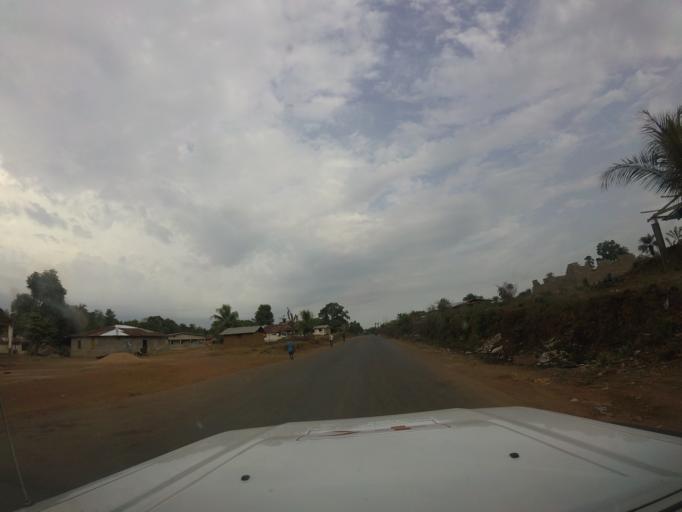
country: LR
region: Bomi
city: Tubmanburg
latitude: 6.7235
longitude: -10.9828
